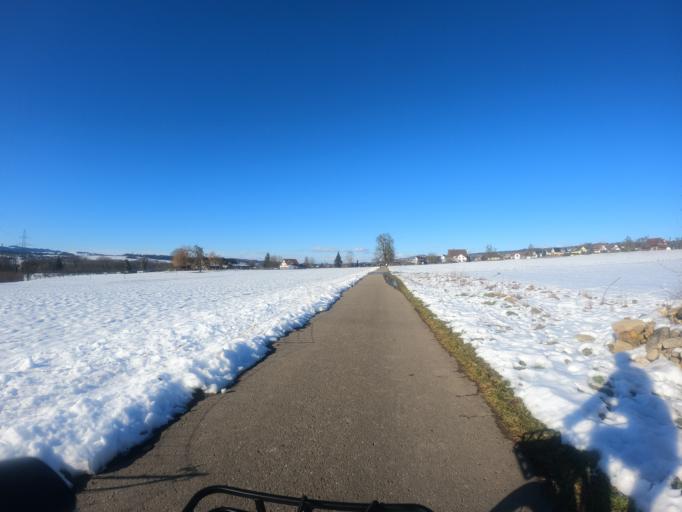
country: CH
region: Aargau
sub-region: Bezirk Bremgarten
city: Jonen
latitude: 47.2910
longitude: 8.3950
